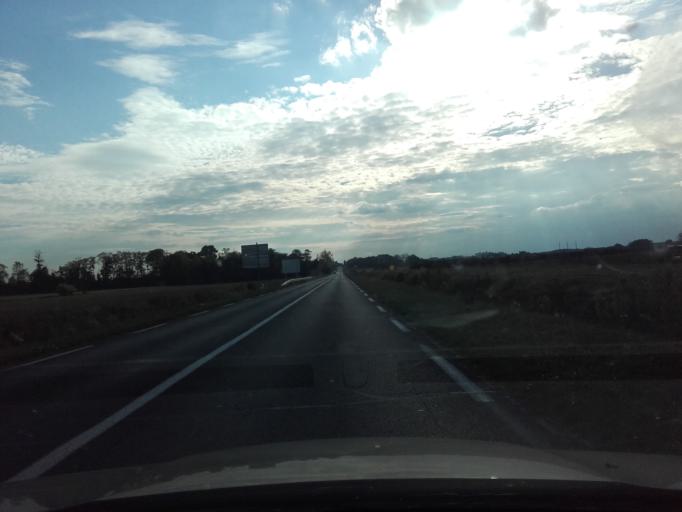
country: FR
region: Centre
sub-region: Departement d'Indre-et-Loire
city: Parcay-Meslay
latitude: 47.4617
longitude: 0.7424
